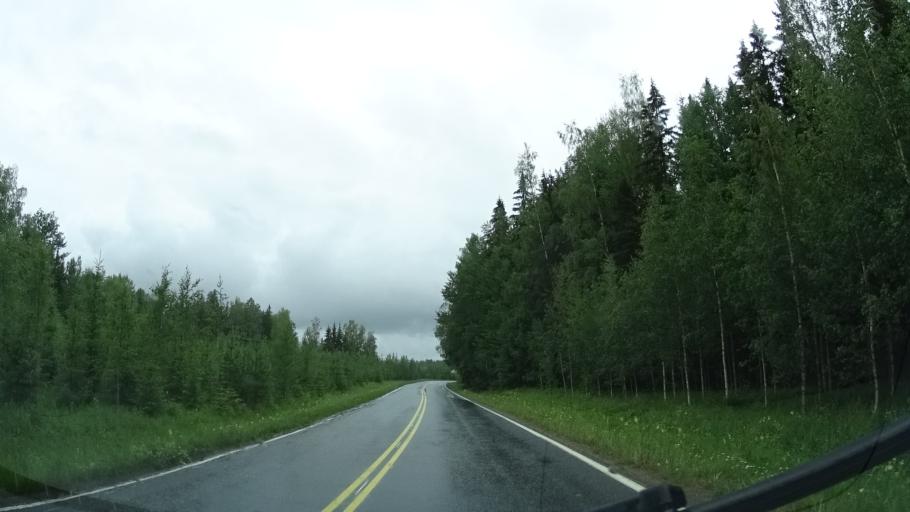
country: FI
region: Haeme
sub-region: Forssa
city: Humppila
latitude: 60.9923
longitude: 23.2567
